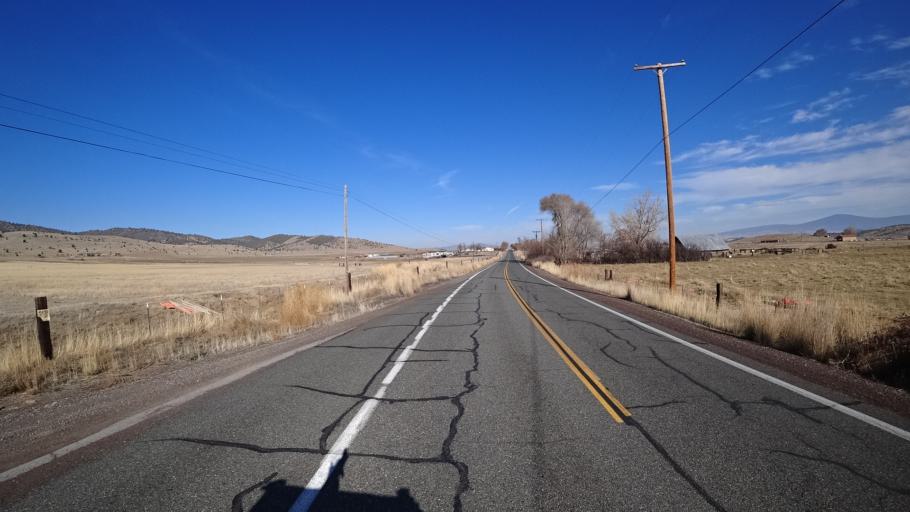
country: US
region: California
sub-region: Siskiyou County
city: Montague
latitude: 41.6095
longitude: -122.5301
